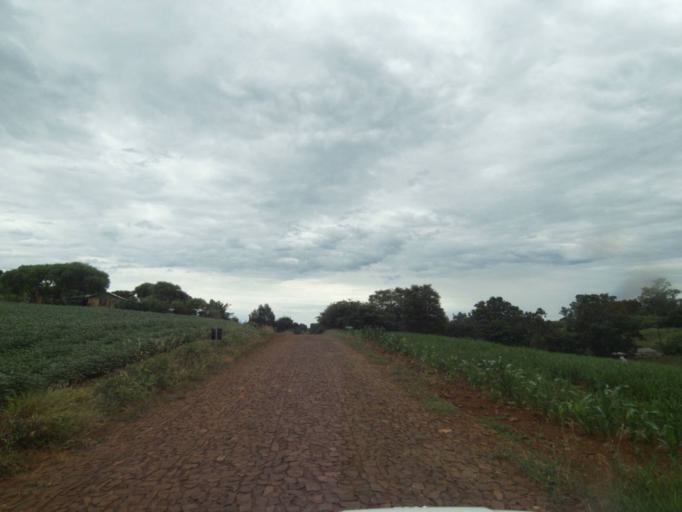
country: BR
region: Parana
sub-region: Guaraniacu
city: Guaraniacu
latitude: -24.9241
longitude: -52.9380
